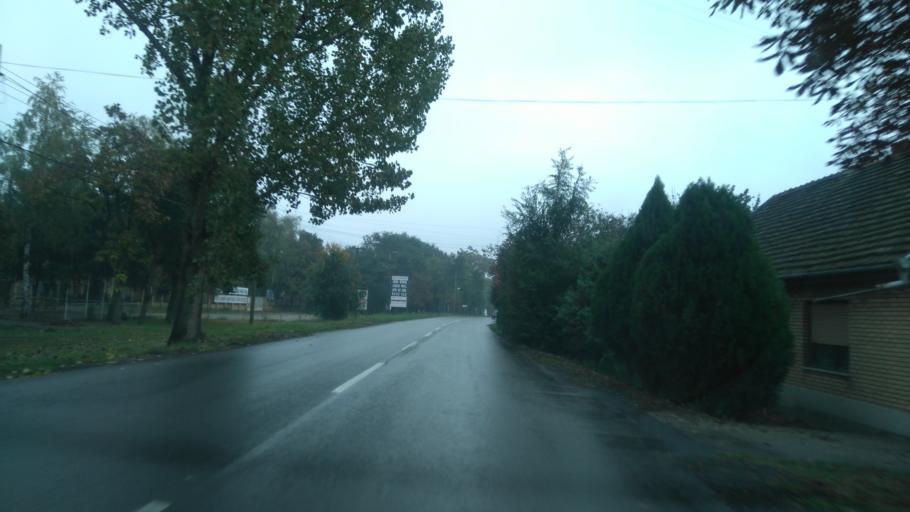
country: RS
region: Autonomna Pokrajina Vojvodina
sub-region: Juznobacki Okrug
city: Becej
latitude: 45.6296
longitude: 20.0344
